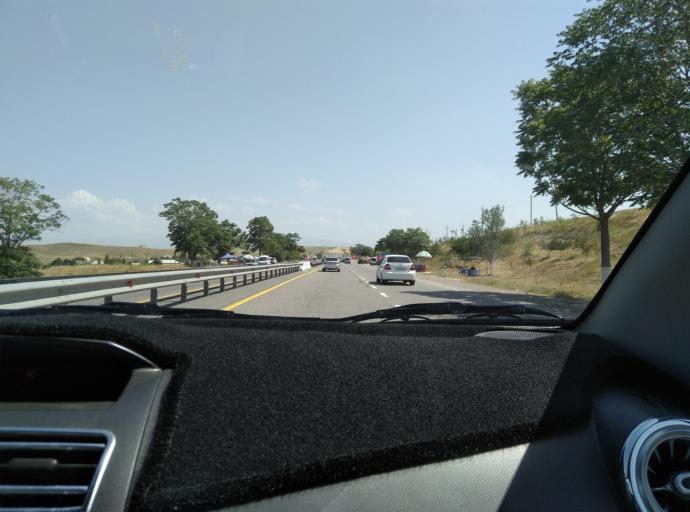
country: UZ
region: Toshkent
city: Ohangaron
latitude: 40.9794
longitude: 69.5413
